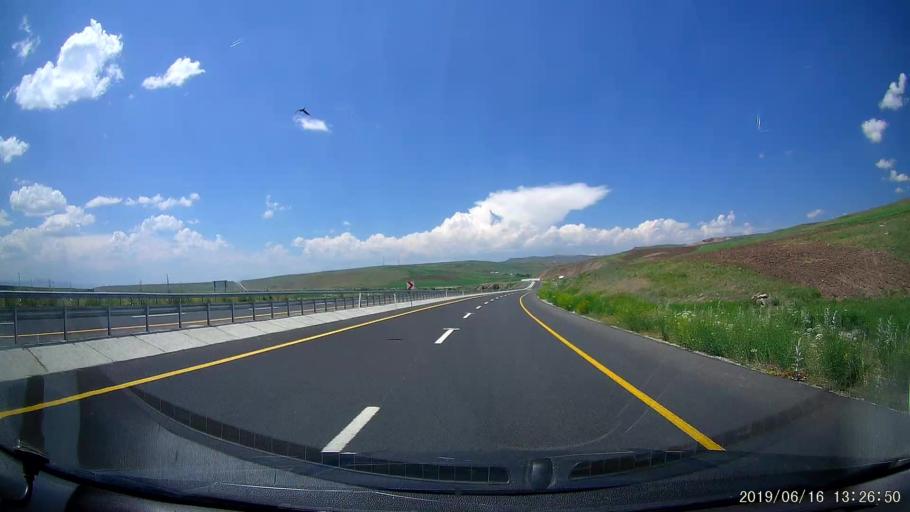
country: TR
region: Agri
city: Taslicay
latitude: 39.6625
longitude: 43.3197
